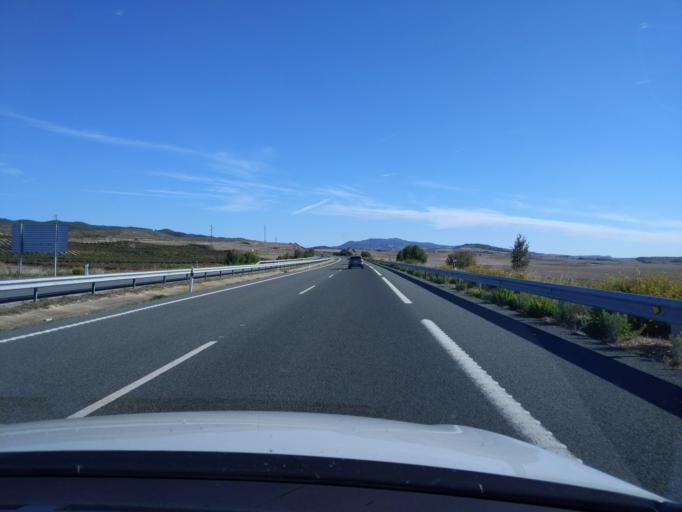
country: ES
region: Navarre
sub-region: Provincia de Navarra
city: Los Arcos
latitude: 42.5684
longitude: -2.1664
